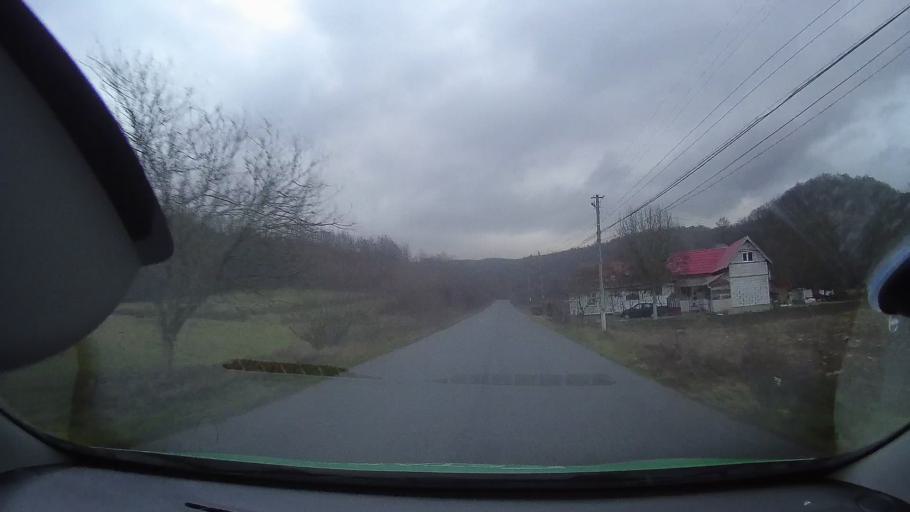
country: RO
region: Hunedoara
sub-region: Comuna Baia de Cris
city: Baia de Cris
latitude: 46.1918
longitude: 22.7159
